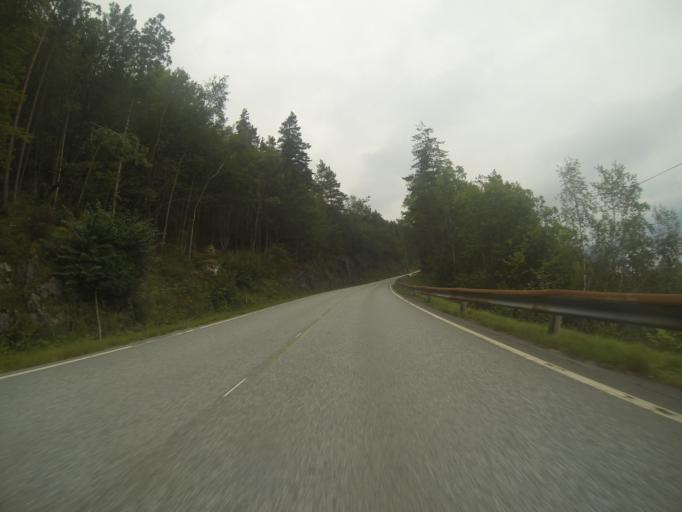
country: NO
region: Rogaland
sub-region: Suldal
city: Sand
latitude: 59.5129
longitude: 6.2242
